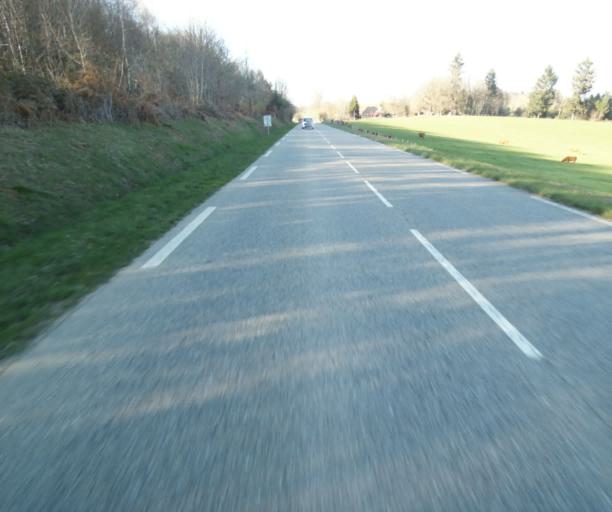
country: FR
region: Limousin
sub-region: Departement de la Correze
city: Seilhac
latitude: 45.3844
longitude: 1.7216
